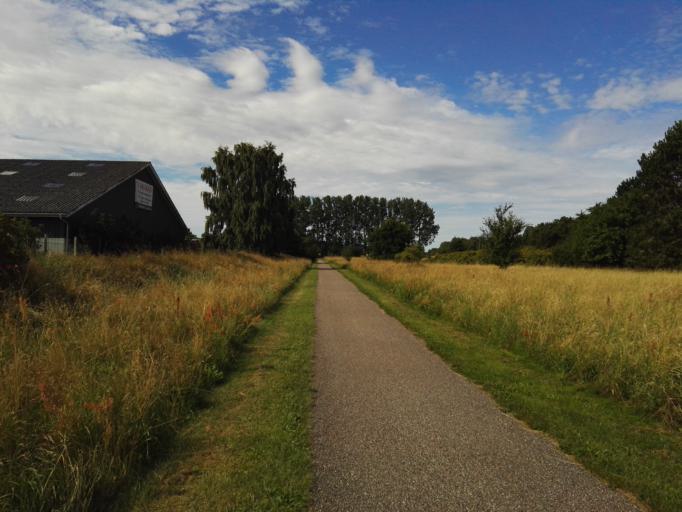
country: DK
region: Zealand
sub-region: Odsherred Kommune
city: Nykobing Sjaelland
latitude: 55.9339
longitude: 11.6720
